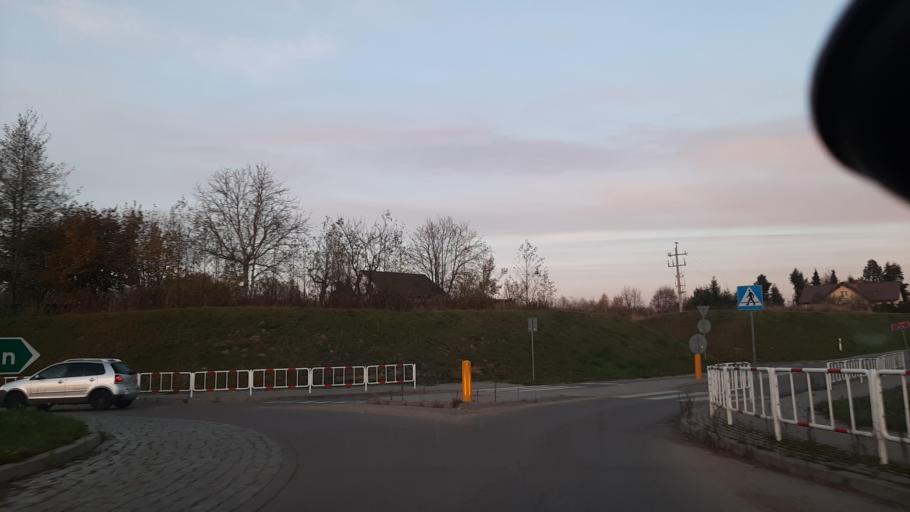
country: PL
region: Lublin Voivodeship
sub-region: Powiat lubelski
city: Jastkow
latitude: 51.3072
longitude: 22.4909
